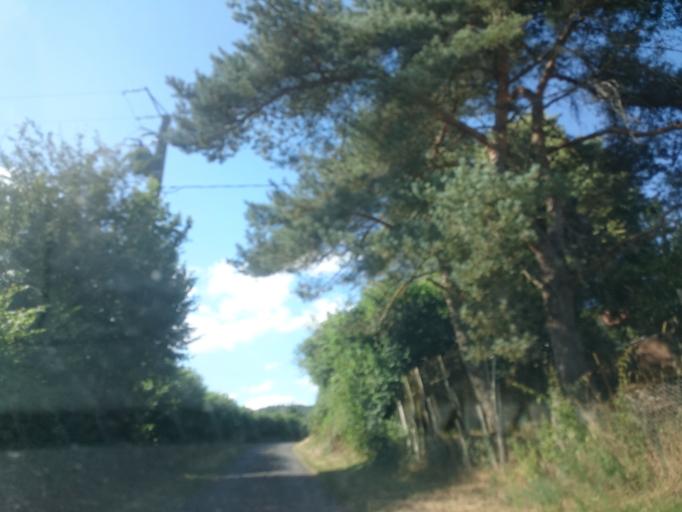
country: FR
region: Auvergne
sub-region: Departement du Cantal
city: Laroquebrou
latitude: 44.8988
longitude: 2.1827
